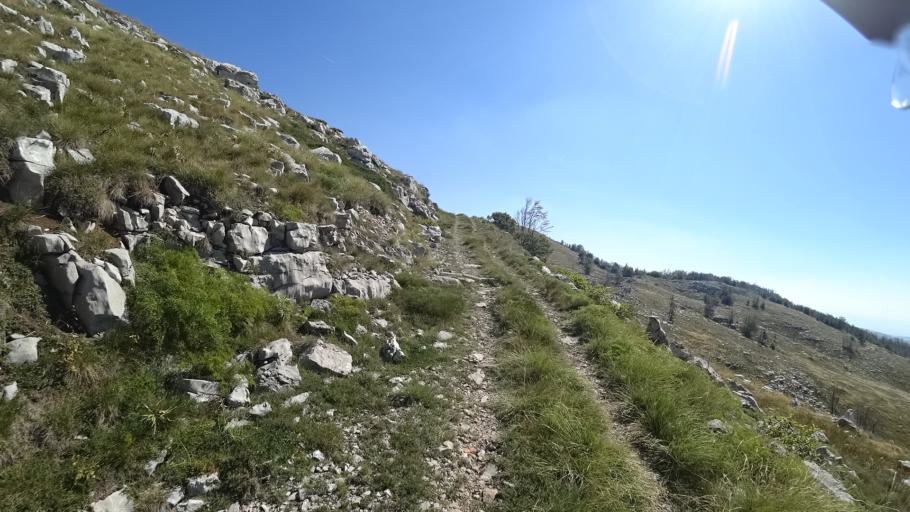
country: HR
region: Splitsko-Dalmatinska
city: Hrvace
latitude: 43.9240
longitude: 16.6064
